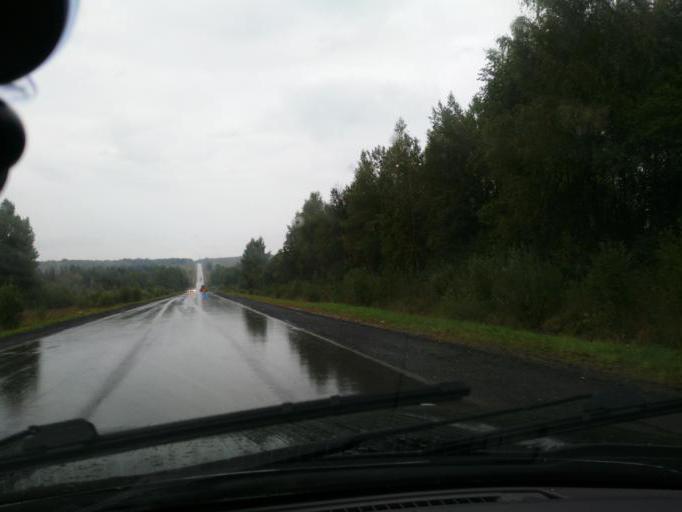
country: RU
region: Perm
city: Yugo-Kamskiy
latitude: 57.4782
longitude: 55.6795
